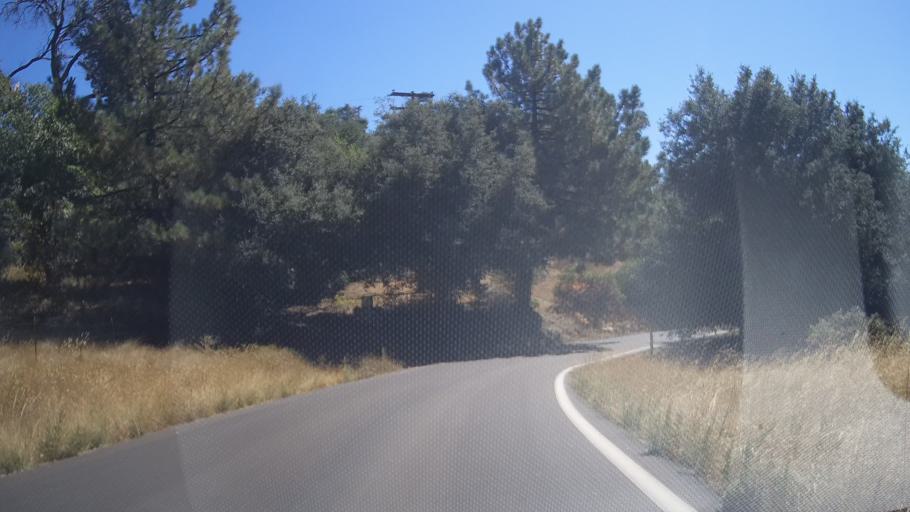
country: US
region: California
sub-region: San Diego County
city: Julian
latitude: 33.0408
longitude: -116.6358
